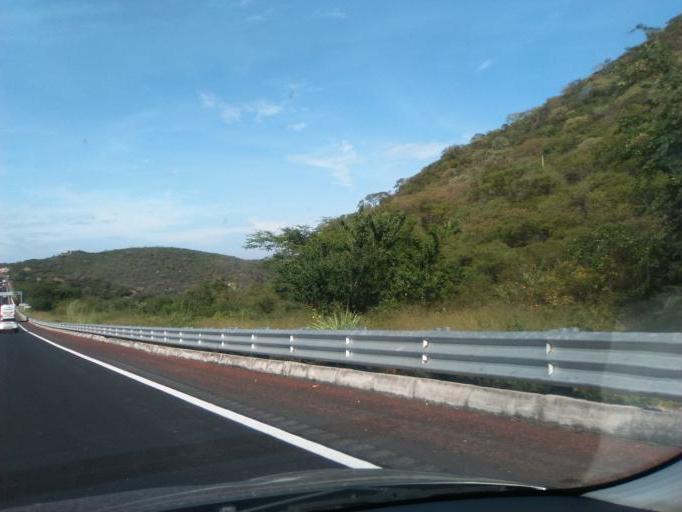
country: MX
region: Morelos
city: Tilzapotla
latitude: 18.4511
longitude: -99.1733
